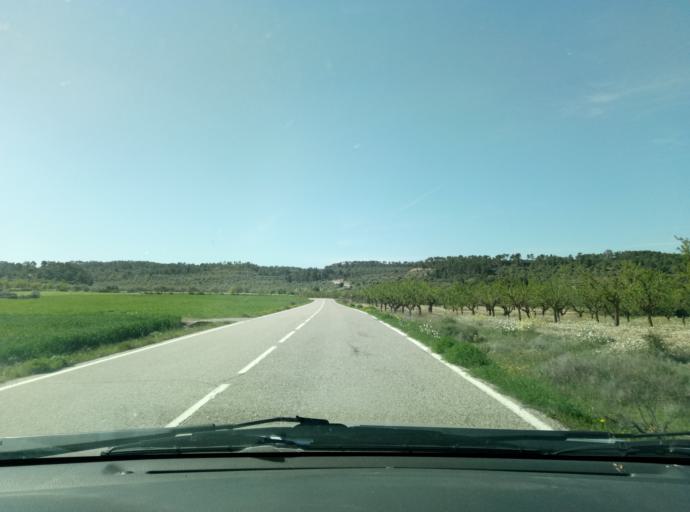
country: ES
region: Catalonia
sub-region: Provincia de Lleida
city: Vallbona de les Monges
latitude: 41.5388
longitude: 1.0273
